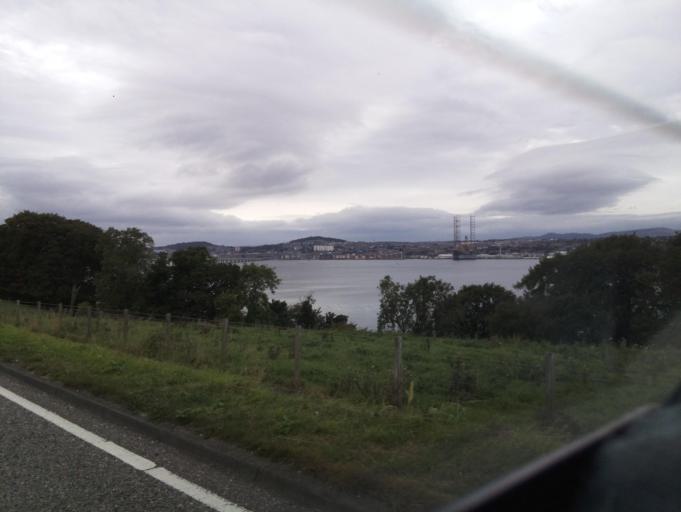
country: GB
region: Scotland
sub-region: Fife
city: Newport-On-Tay
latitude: 56.4491
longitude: -2.9243
